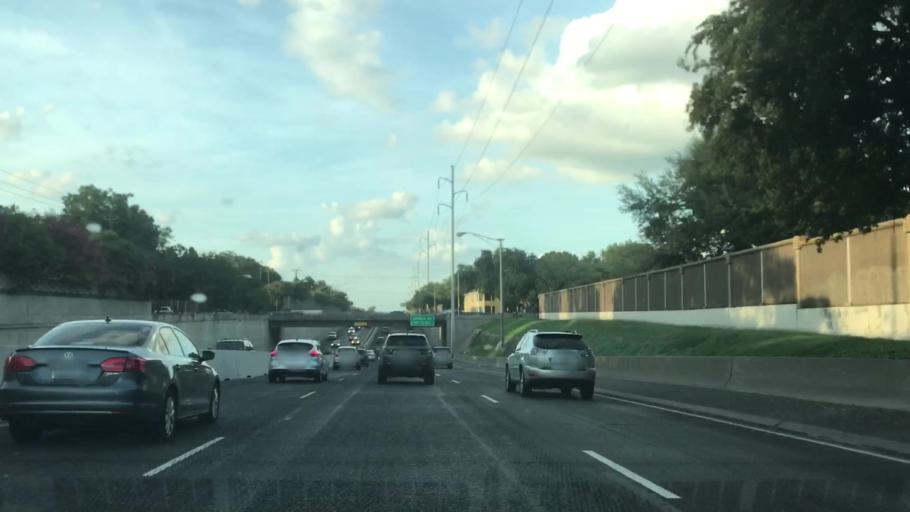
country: US
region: Texas
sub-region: Dallas County
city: University Park
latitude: 32.8441
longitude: -96.8140
